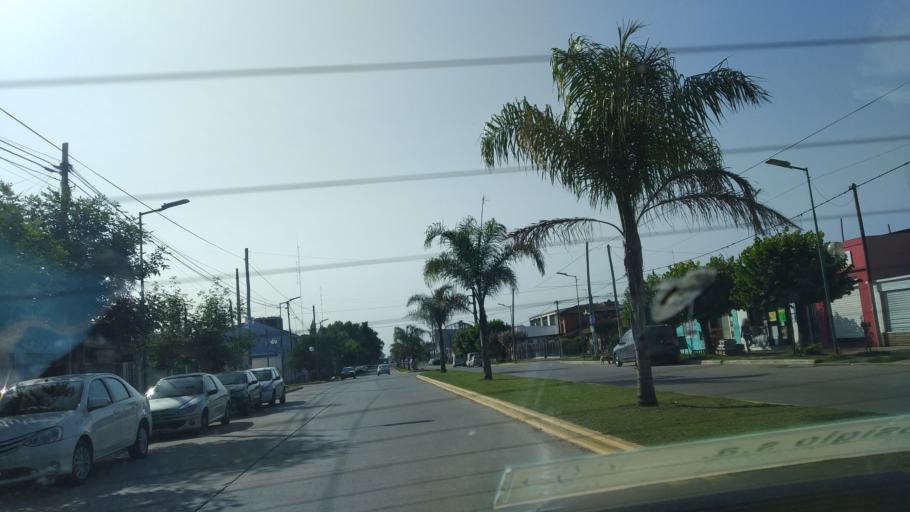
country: AR
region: Buenos Aires
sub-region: Partido de La Plata
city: La Plata
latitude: -34.9966
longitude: -58.0465
